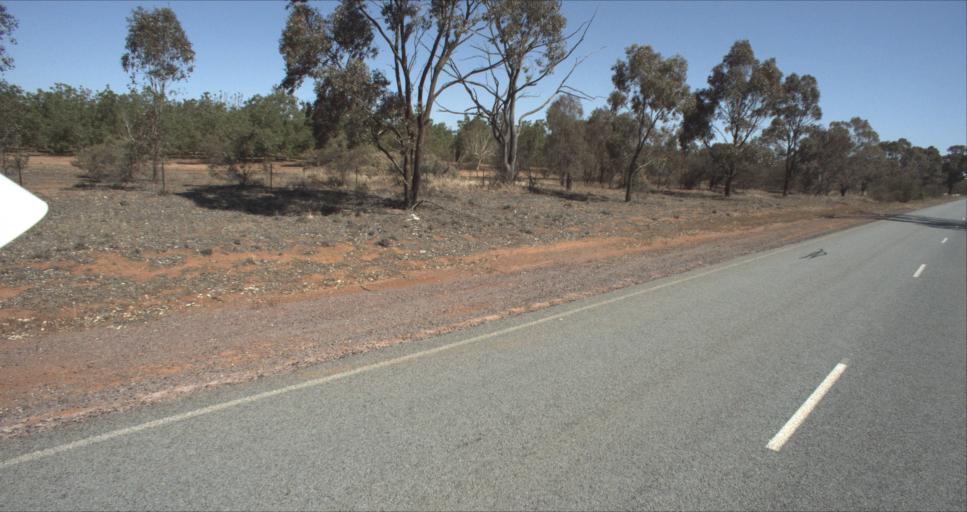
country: AU
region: New South Wales
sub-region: Leeton
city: Leeton
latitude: -34.4922
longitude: 146.4627
